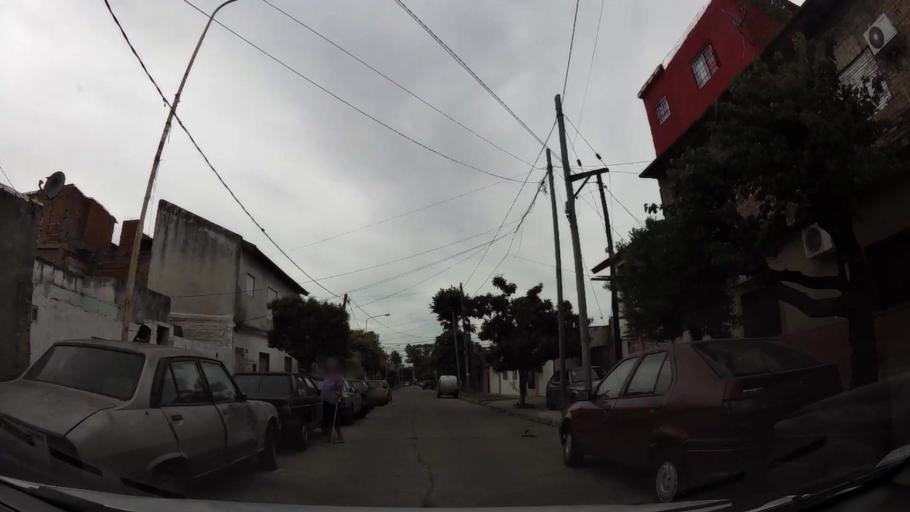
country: AR
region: Buenos Aires
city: San Justo
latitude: -34.6726
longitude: -58.5187
